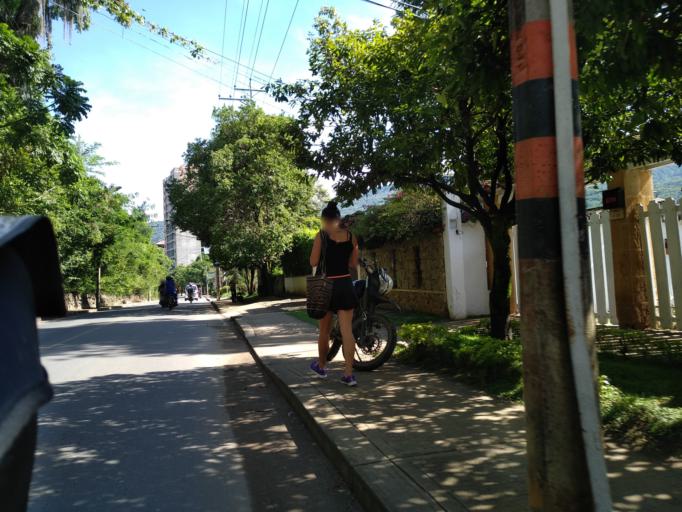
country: CO
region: Santander
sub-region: San Gil
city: San Gil
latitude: 6.5471
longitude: -73.1288
